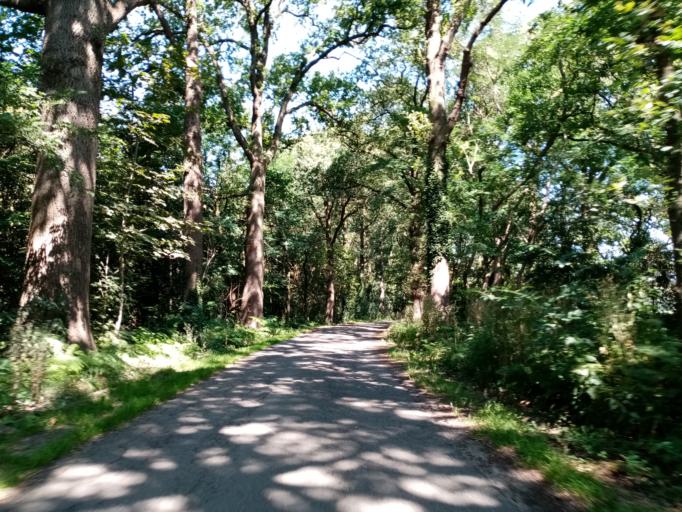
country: NL
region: North Brabant
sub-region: Gemeente Breda
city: Breda
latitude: 51.6104
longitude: 4.7320
